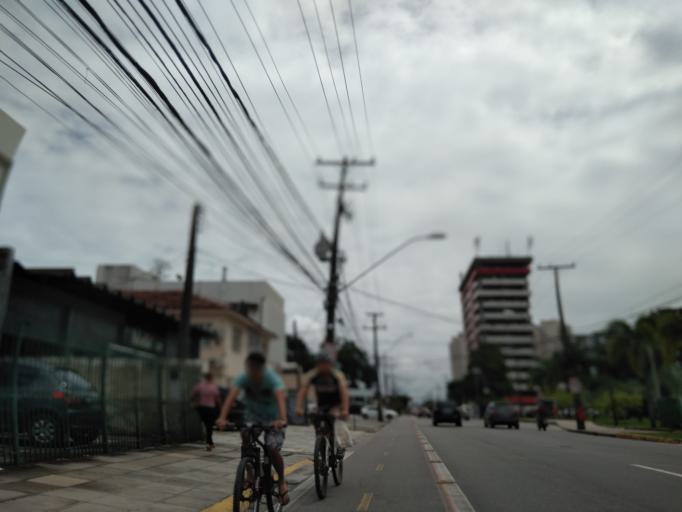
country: BR
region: Pernambuco
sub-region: Recife
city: Recife
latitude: -8.1117
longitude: -34.9037
